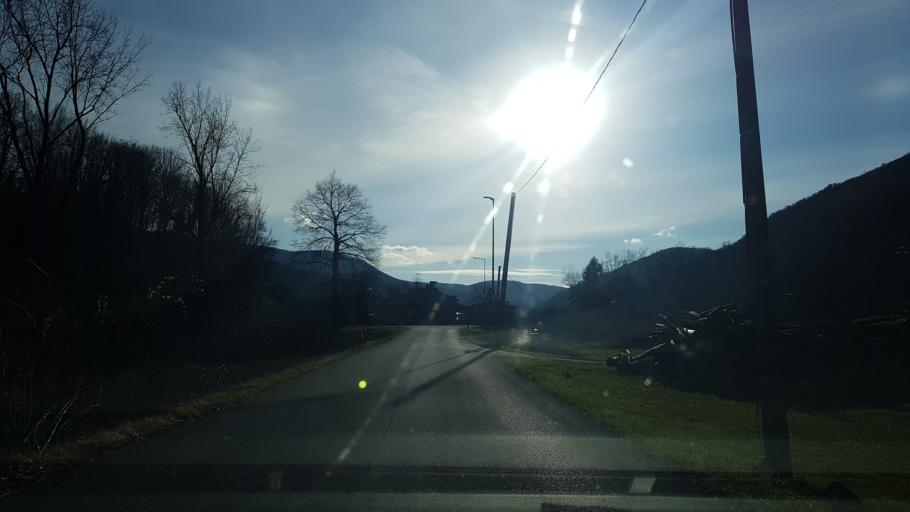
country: IT
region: Friuli Venezia Giulia
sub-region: Provincia di Udine
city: Merso di Sopra
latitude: 46.1352
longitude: 13.5373
